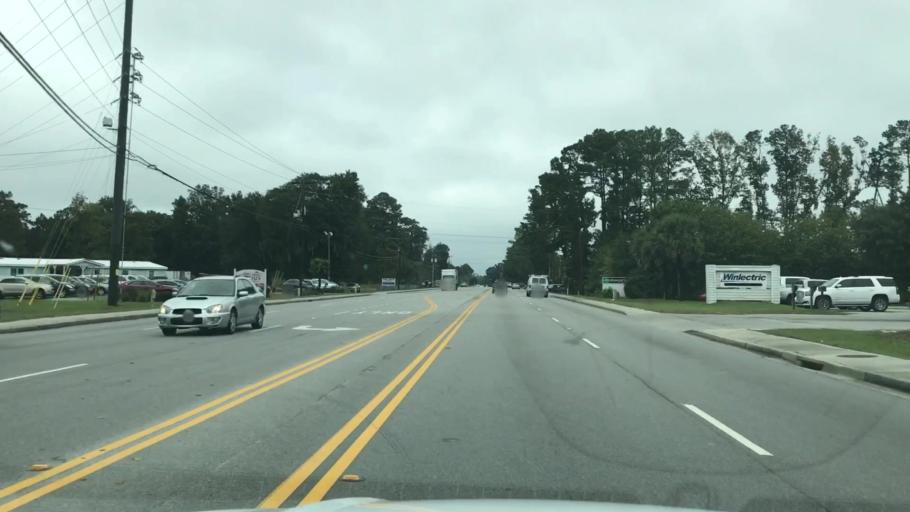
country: US
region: South Carolina
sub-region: Beaufort County
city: Burton
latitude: 32.4280
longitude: -80.7231
